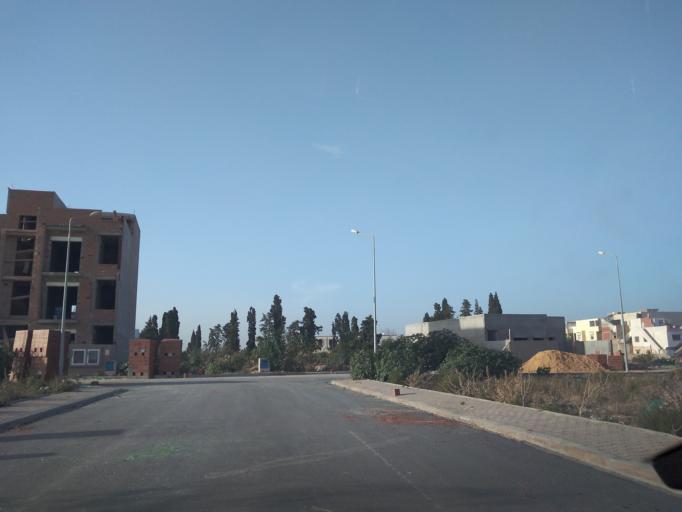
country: TN
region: Manouba
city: Manouba
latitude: 36.7962
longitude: 10.0869
